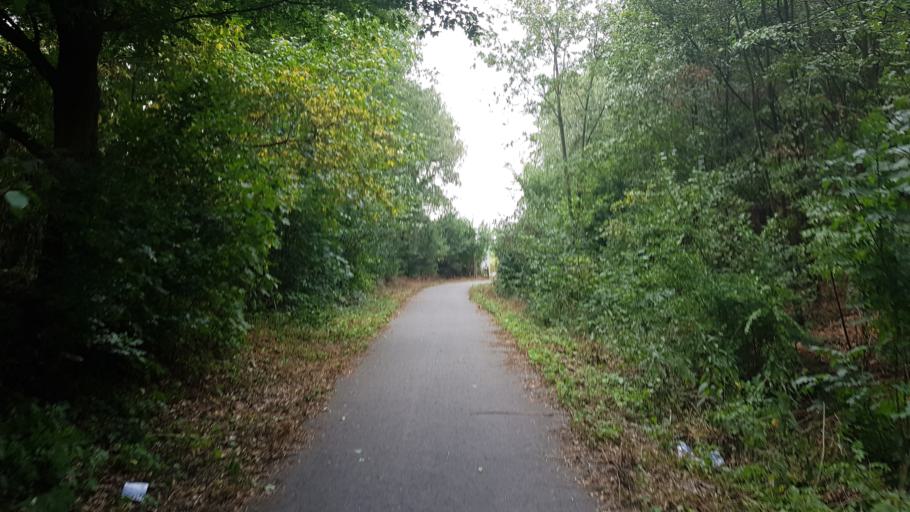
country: DE
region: North Rhine-Westphalia
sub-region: Regierungsbezirk Dusseldorf
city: Kamp-Lintfort
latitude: 51.4656
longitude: 6.5674
